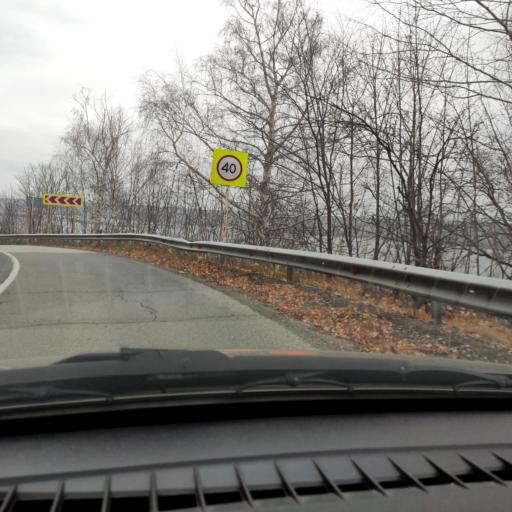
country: RU
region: Samara
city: Pribrezhnyy
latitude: 53.4417
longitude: 49.7726
